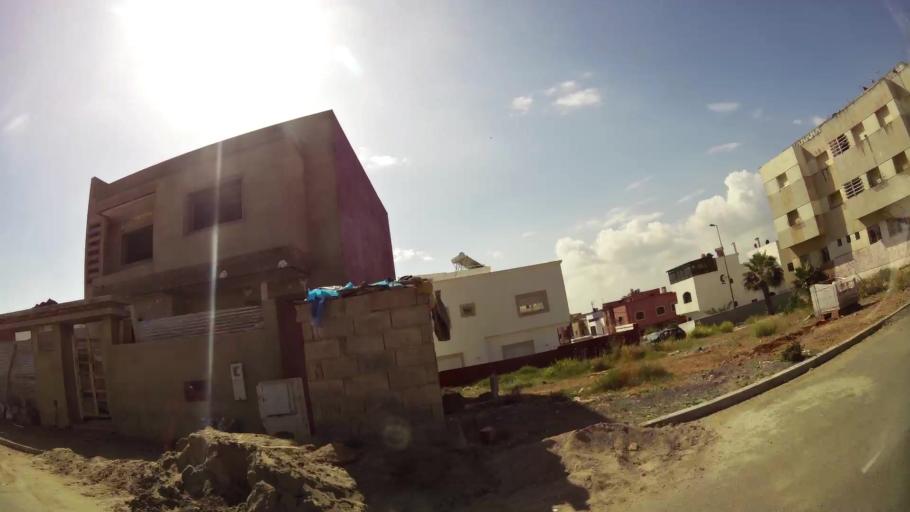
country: MA
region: Rabat-Sale-Zemmour-Zaer
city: Sale
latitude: 34.0657
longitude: -6.8060
